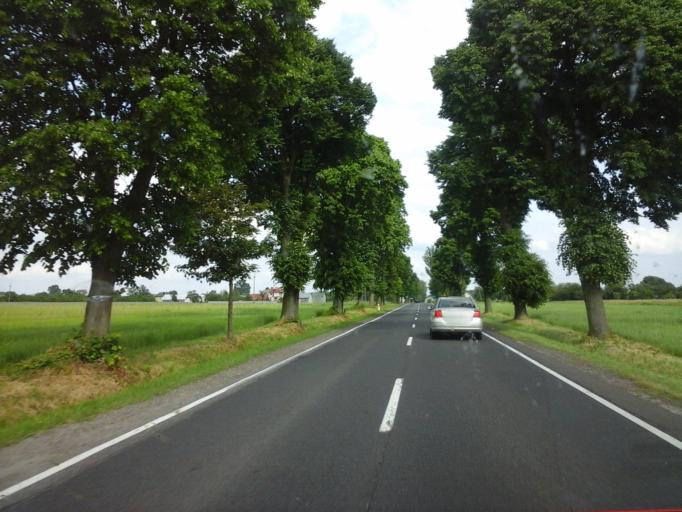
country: PL
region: Lodz Voivodeship
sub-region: Powiat opoczynski
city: Mniszkow
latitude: 51.3321
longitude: 20.0232
